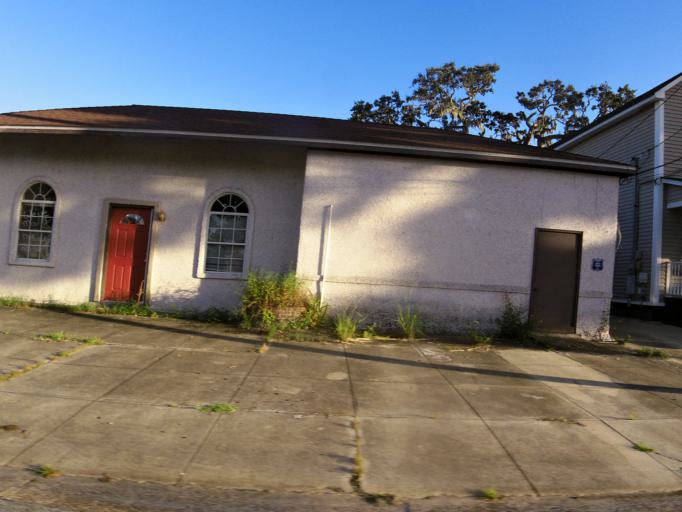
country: US
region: Georgia
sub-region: Glynn County
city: Brunswick
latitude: 31.1527
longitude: -81.4928
